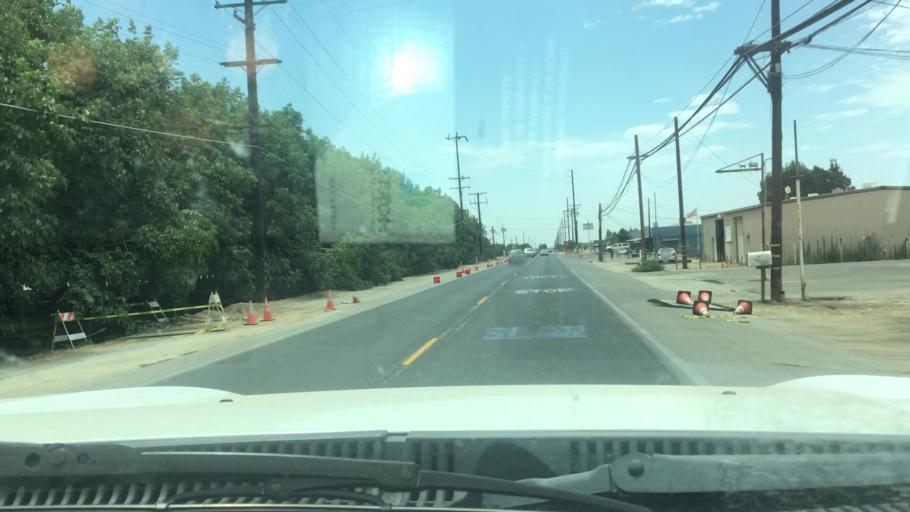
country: US
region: California
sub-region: Tulare County
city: Poplar-Cotton Center
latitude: 36.0658
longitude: -119.1052
